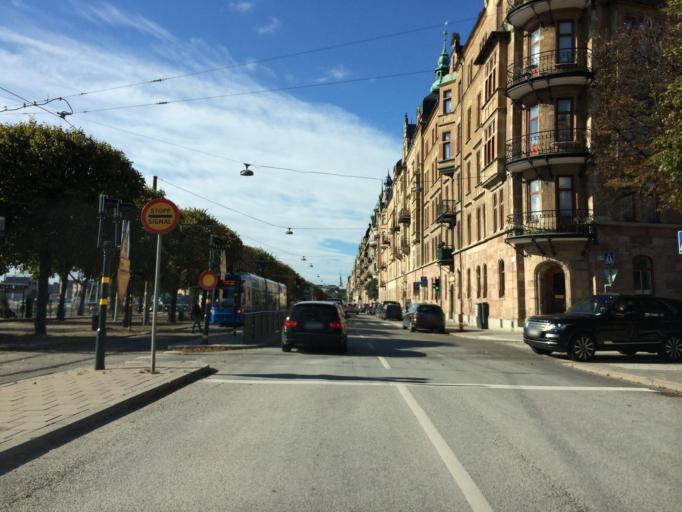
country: SE
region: Stockholm
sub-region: Stockholms Kommun
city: OEstermalm
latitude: 59.3320
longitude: 18.0934
